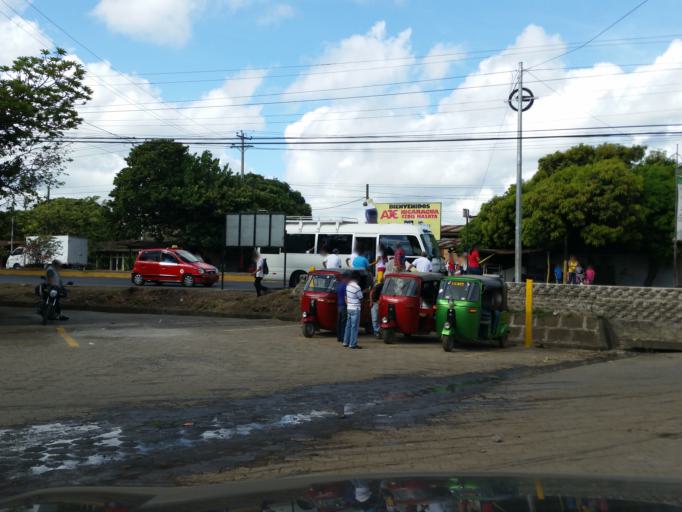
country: NI
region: Masaya
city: Masaya
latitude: 11.9867
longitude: -86.0936
